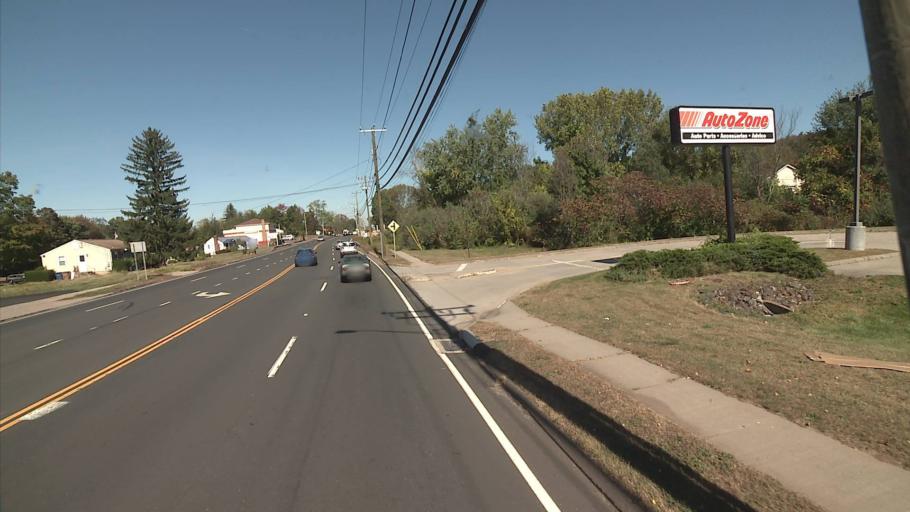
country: US
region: Connecticut
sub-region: Tolland County
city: Rockville
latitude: 41.8329
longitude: -72.4932
